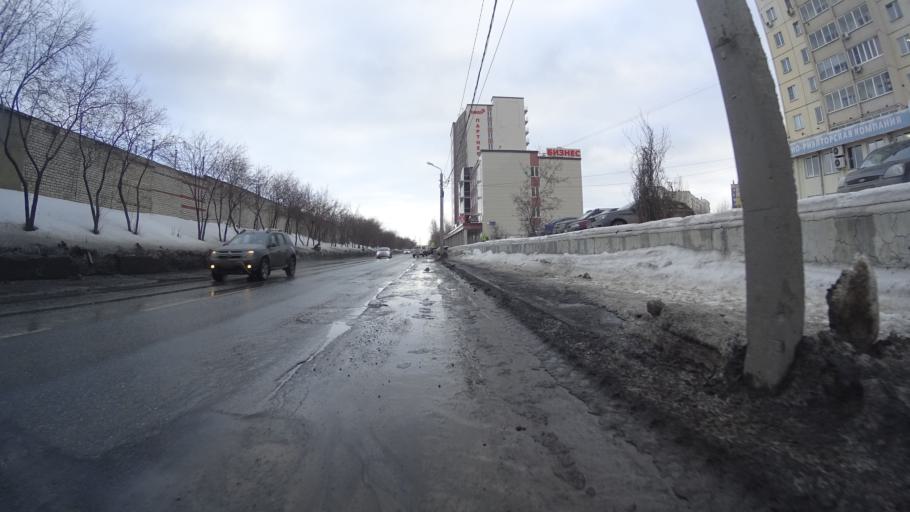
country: RU
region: Chelyabinsk
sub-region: Gorod Chelyabinsk
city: Chelyabinsk
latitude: 55.1435
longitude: 61.4008
